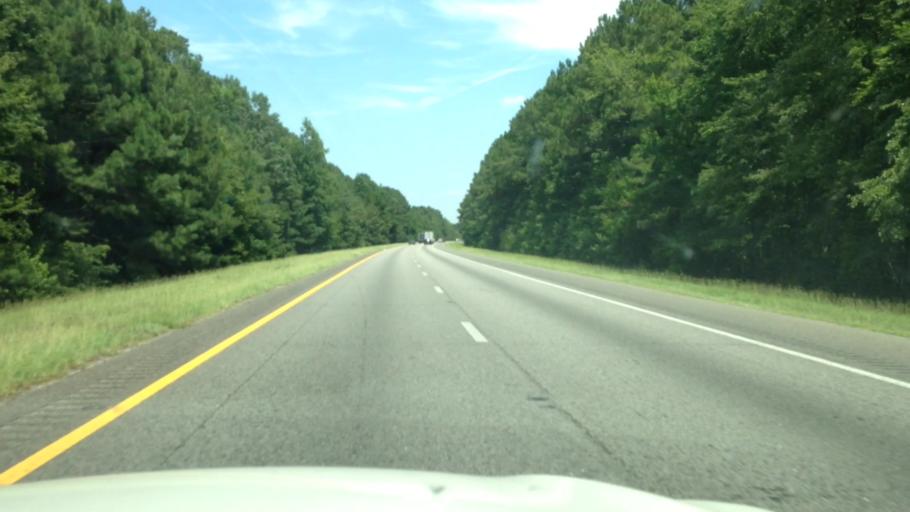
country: US
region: South Carolina
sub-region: Florence County
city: Florence
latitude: 34.3088
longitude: -79.6166
